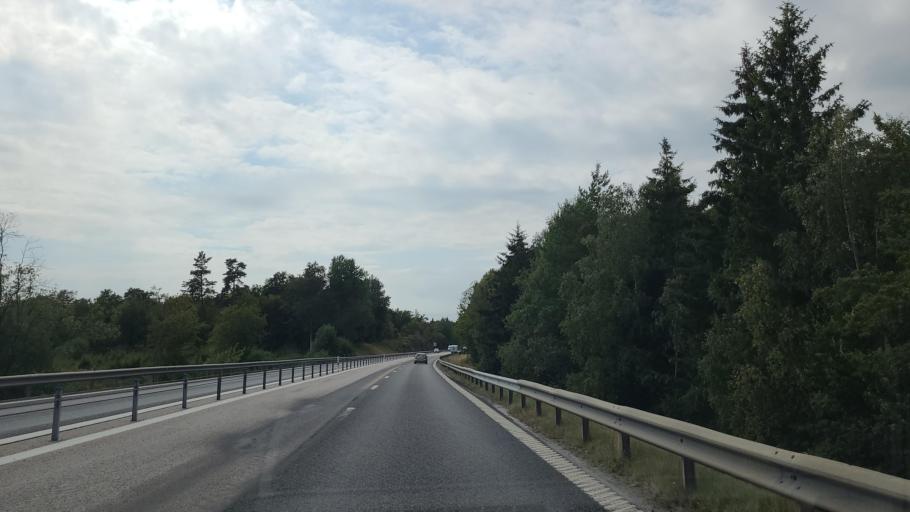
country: SE
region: Blekinge
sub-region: Ronneby Kommun
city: Ronneby
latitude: 56.2187
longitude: 15.1989
